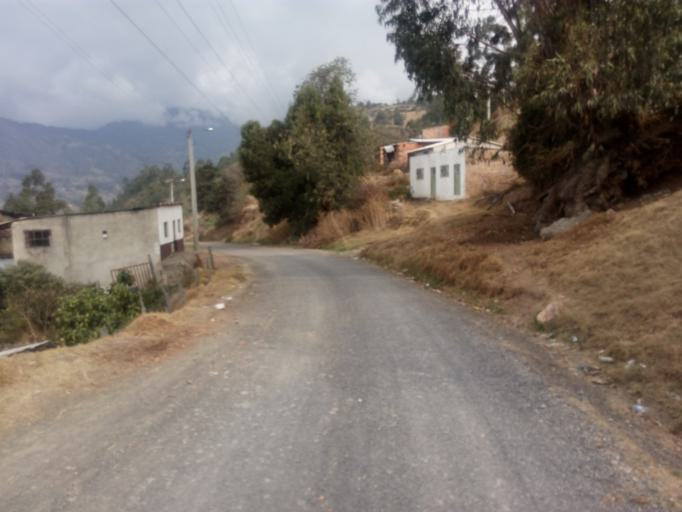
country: CO
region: Boyaca
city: Chita
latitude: 6.1895
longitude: -72.4750
